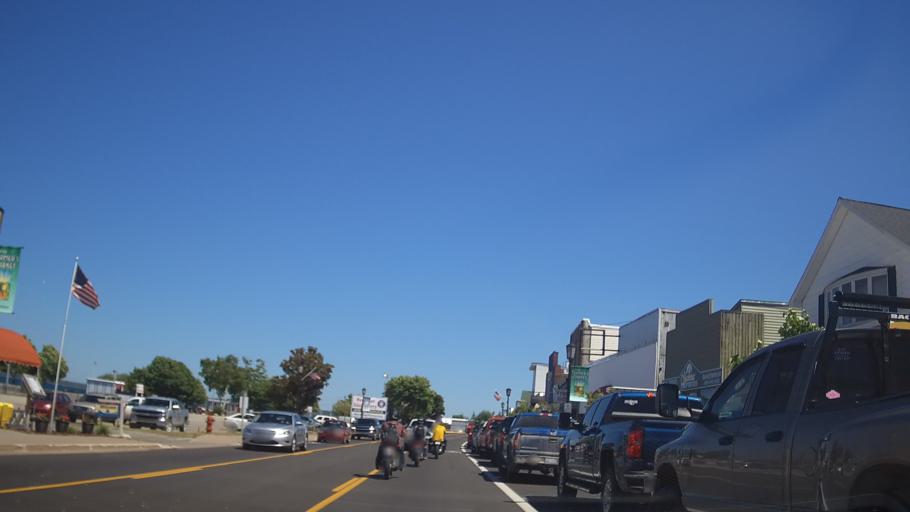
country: US
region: Michigan
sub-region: Mackinac County
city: Saint Ignace
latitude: 45.8685
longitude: -84.7263
